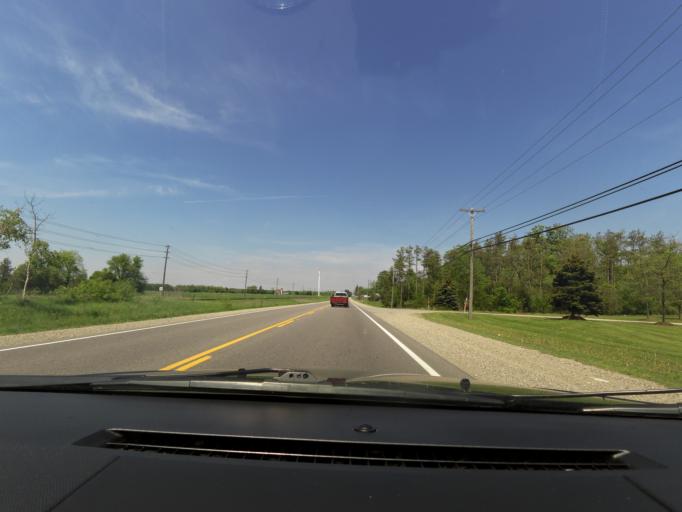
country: CA
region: Ontario
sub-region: Wellington County
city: Guelph
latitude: 43.5840
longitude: -80.1834
